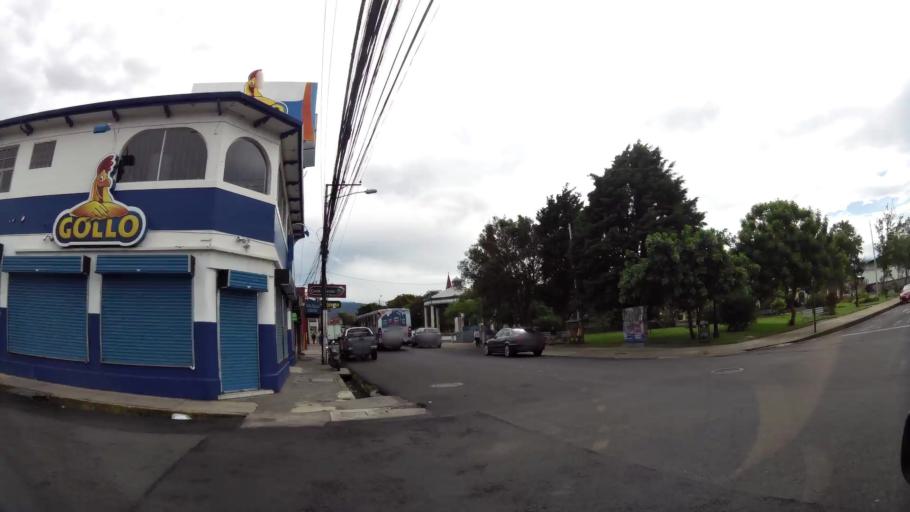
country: CR
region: San Jose
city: San Vicente de Moravia
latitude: 9.9623
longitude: -84.0496
